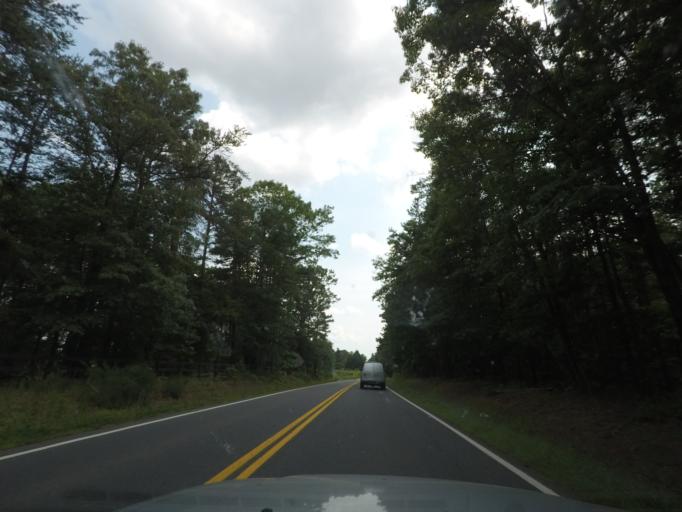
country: US
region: Virginia
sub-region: Fluvanna County
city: Palmyra
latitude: 37.9389
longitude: -78.2457
